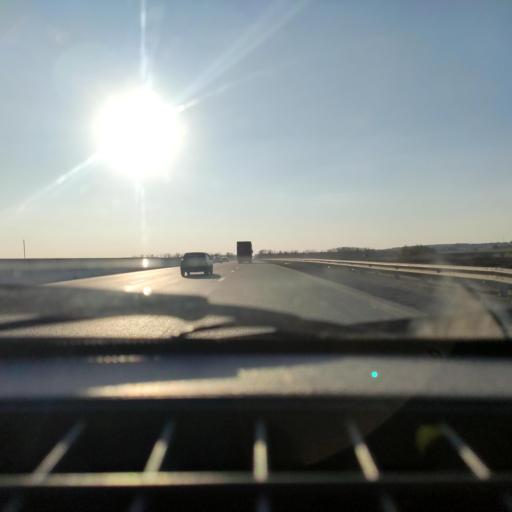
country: RU
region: Bashkortostan
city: Avdon
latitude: 54.6727
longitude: 55.7751
